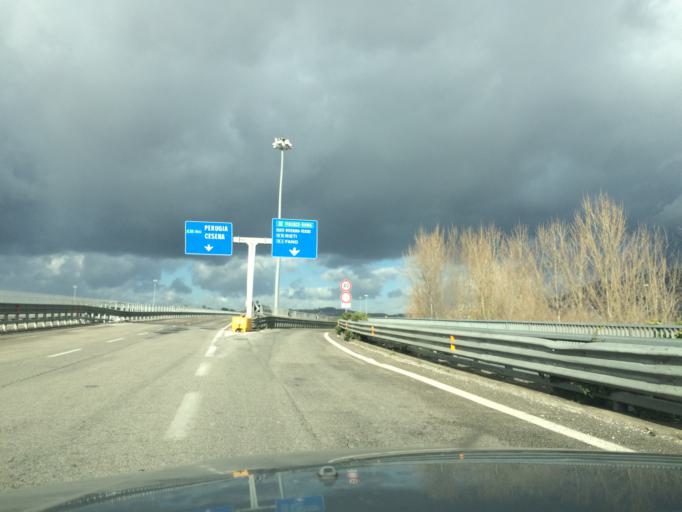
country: IT
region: Umbria
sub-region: Provincia di Terni
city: San Gemini
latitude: 42.5661
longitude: 12.5784
